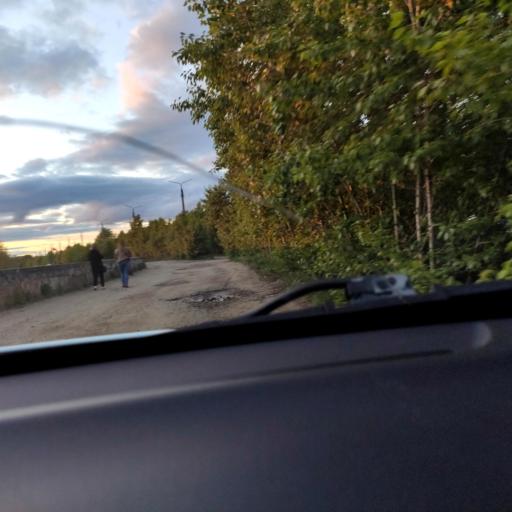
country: RU
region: Tatarstan
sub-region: Gorod Kazan'
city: Kazan
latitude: 55.7827
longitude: 49.0980
